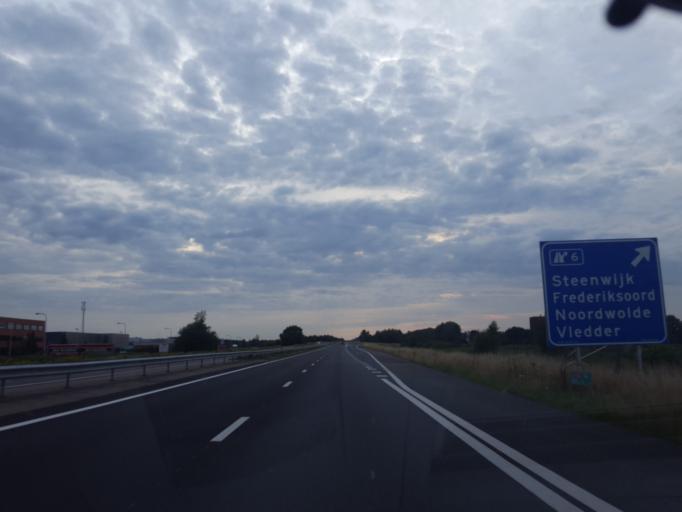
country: NL
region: Overijssel
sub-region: Gemeente Steenwijkerland
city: Steenwijk
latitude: 52.7974
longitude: 6.1366
